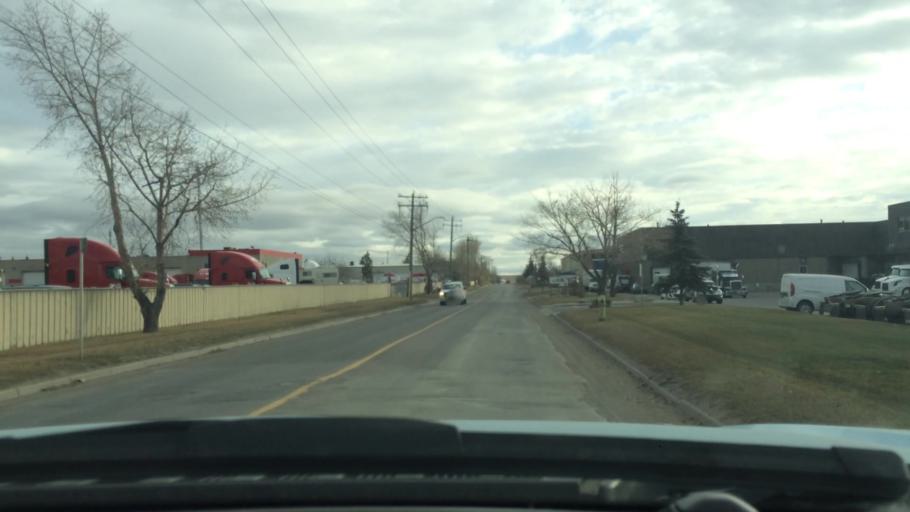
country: CA
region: Alberta
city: Calgary
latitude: 51.0038
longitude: -113.9668
